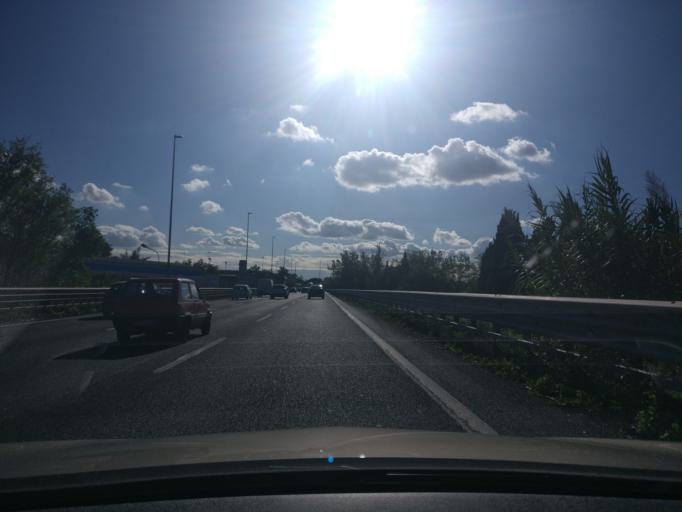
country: IT
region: Latium
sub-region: Citta metropolitana di Roma Capitale
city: Ciampino
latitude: 41.8299
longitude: 12.5827
